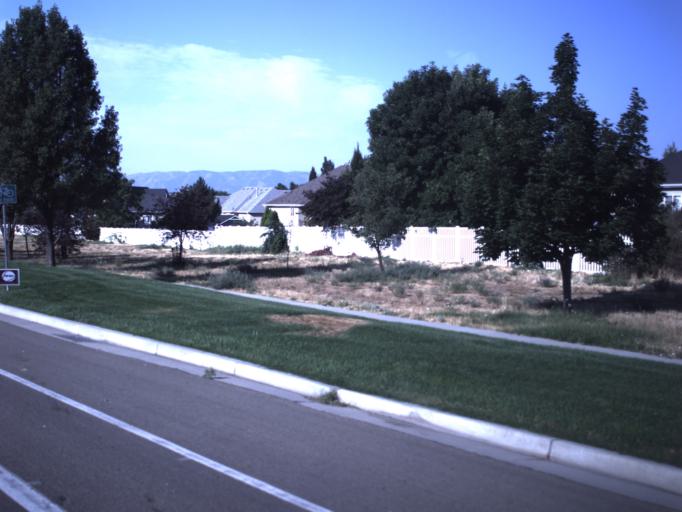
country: US
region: Utah
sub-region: Utah County
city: Cedar Hills
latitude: 40.4119
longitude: -111.7887
